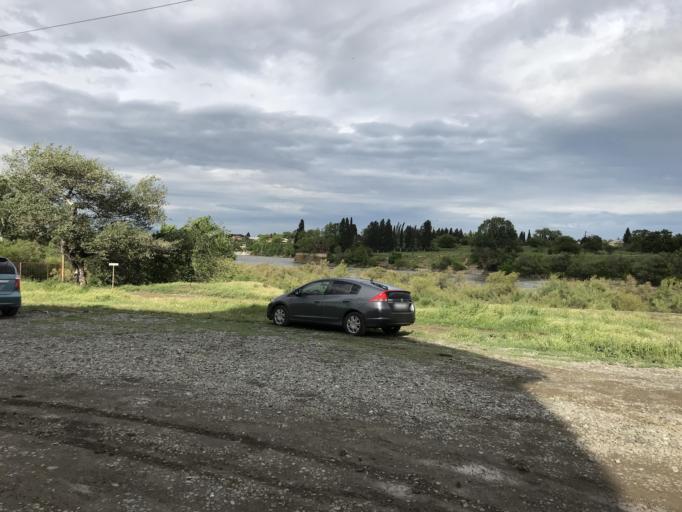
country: GE
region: Kvemo Kartli
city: Rust'avi
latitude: 41.5479
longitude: 45.0019
